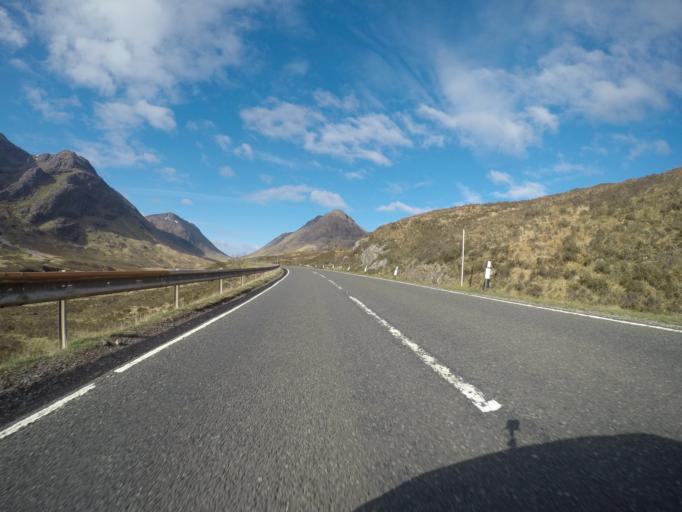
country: GB
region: Scotland
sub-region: Highland
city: Spean Bridge
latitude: 56.6644
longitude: -4.9070
